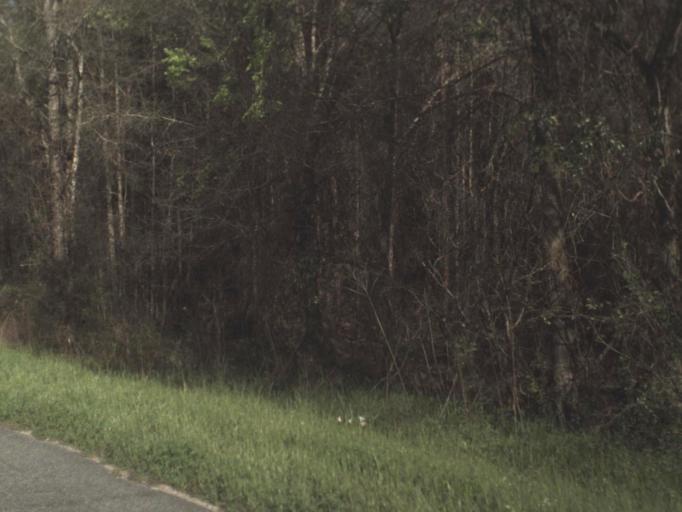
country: US
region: Florida
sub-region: Jackson County
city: Malone
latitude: 30.9762
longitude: -85.0168
